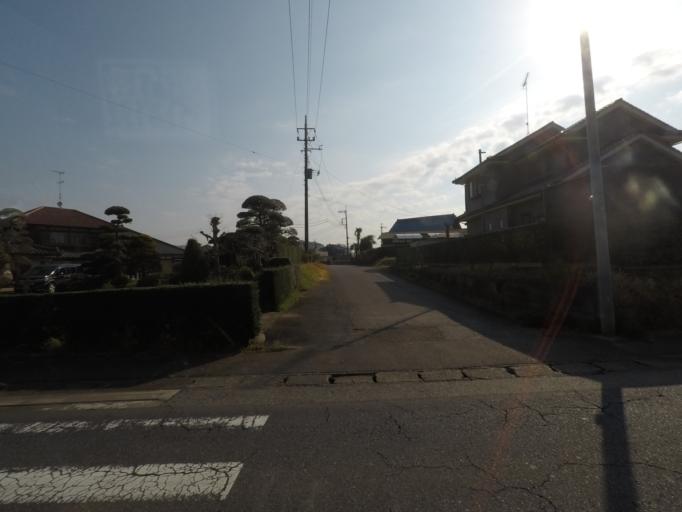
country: JP
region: Chiba
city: Shisui
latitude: 35.7215
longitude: 140.3129
